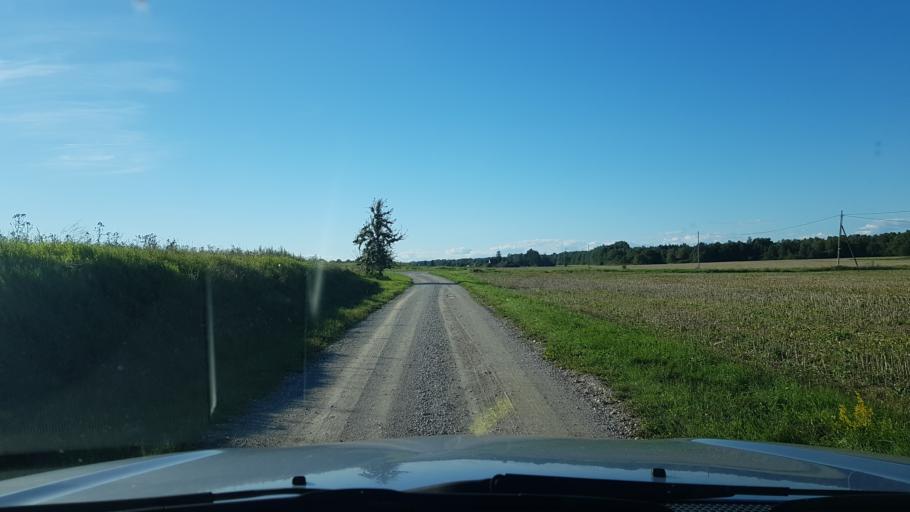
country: EE
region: Harju
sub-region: Rae vald
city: Jueri
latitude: 59.3846
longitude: 24.8813
